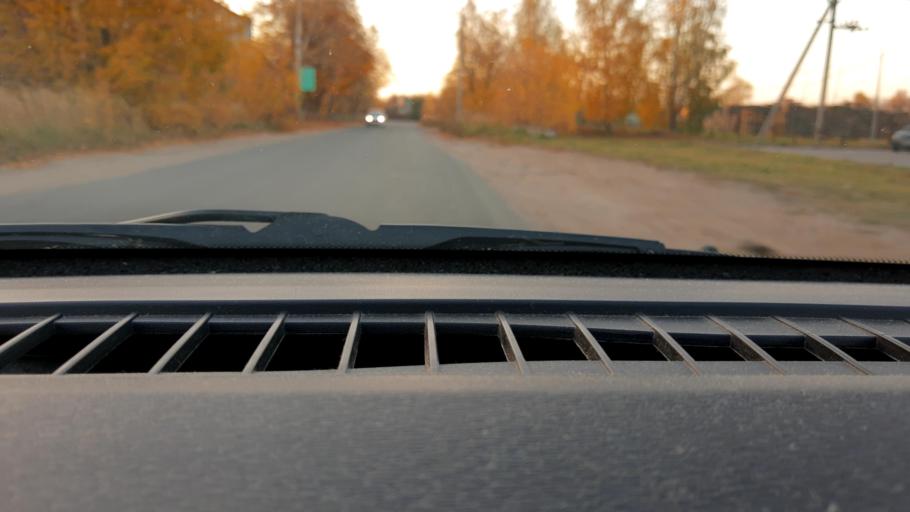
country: RU
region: Nizjnij Novgorod
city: Kstovo
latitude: 56.1881
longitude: 44.1552
